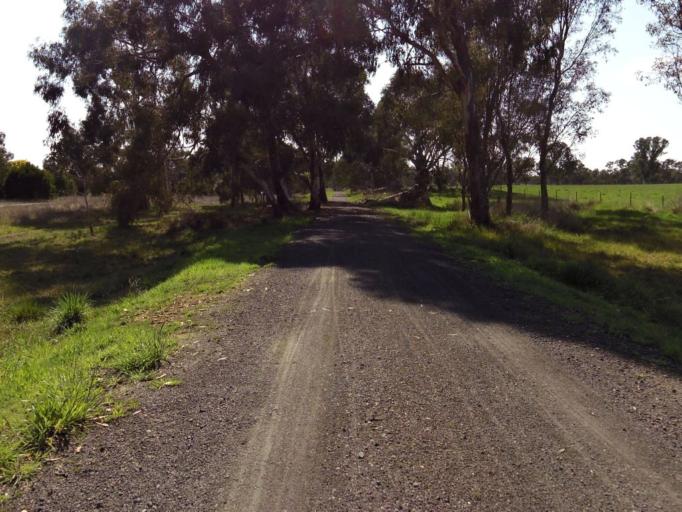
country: AU
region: Victoria
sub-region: Murrindindi
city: Alexandra
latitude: -37.1225
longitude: 145.6009
